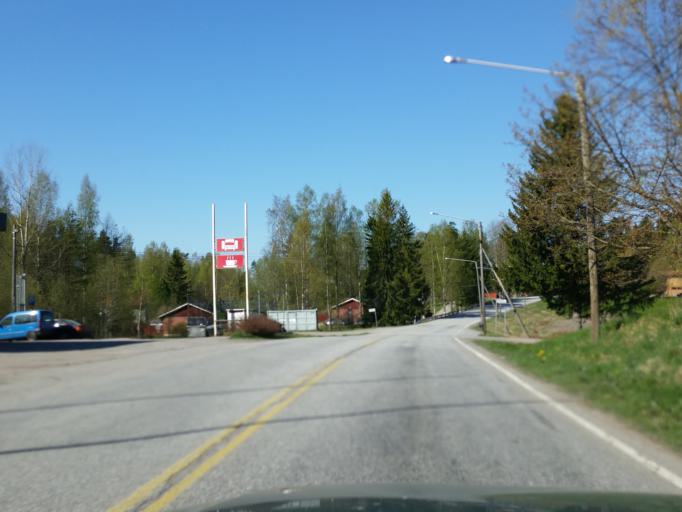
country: FI
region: Uusimaa
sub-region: Helsinki
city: Siuntio
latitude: 60.1693
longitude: 24.1928
